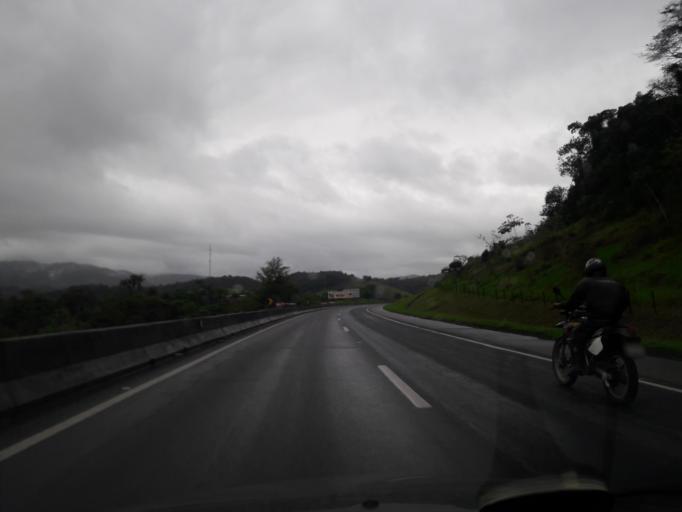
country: BR
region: Sao Paulo
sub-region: Miracatu
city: Miracatu
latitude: -24.2055
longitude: -47.3721
